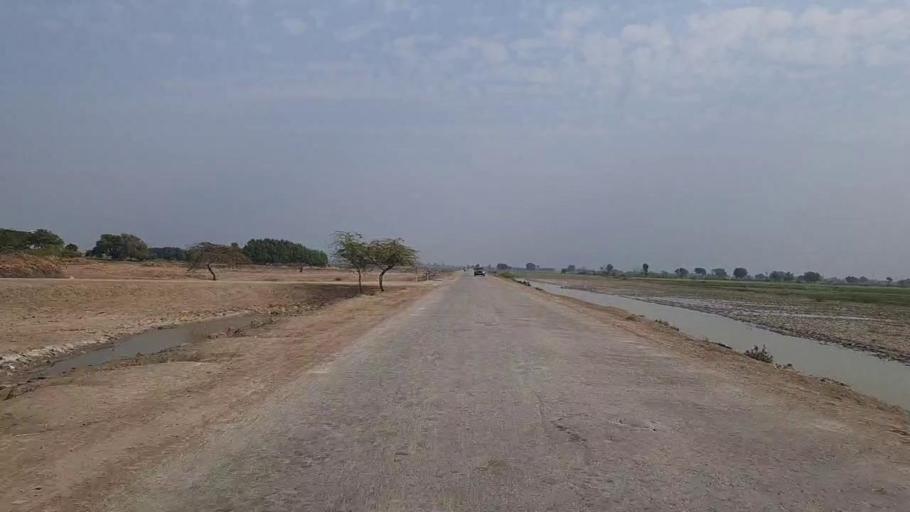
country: PK
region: Sindh
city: Mirwah Gorchani
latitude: 25.4110
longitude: 69.0392
